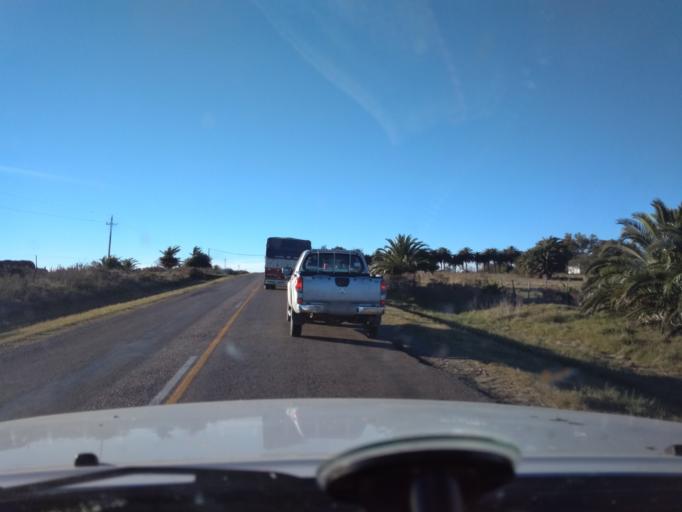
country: UY
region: Canelones
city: San Ramon
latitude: -34.1595
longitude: -55.9469
